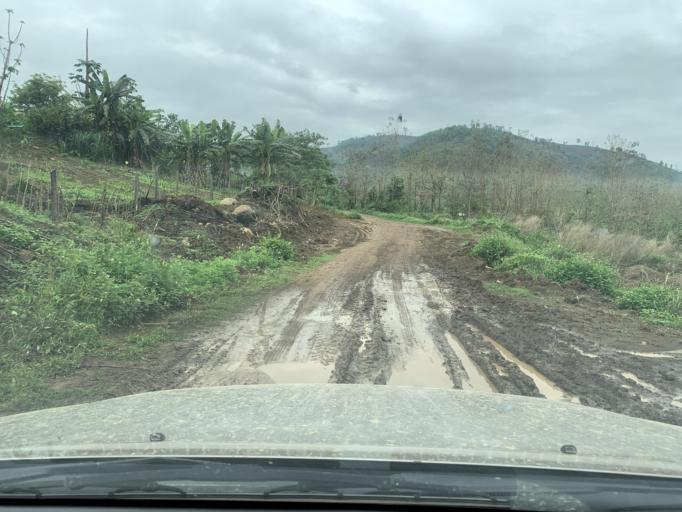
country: TH
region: Uttaradit
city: Ban Khok
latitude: 18.3950
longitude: 101.4296
